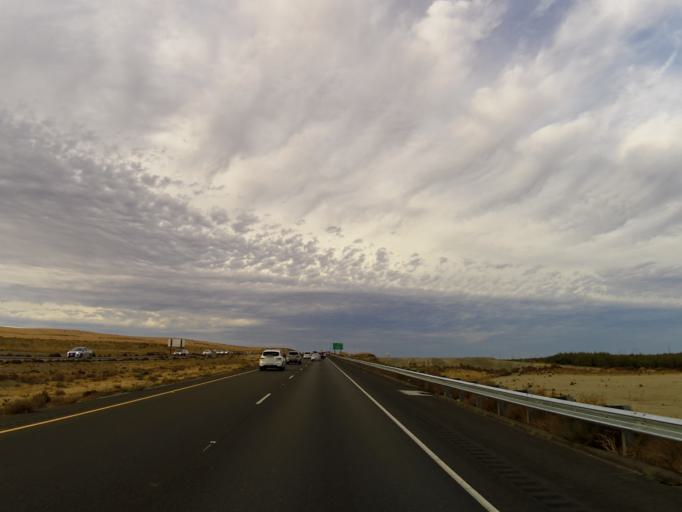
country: US
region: California
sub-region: Kings County
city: Kettleman City
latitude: 35.9619
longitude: -119.9398
